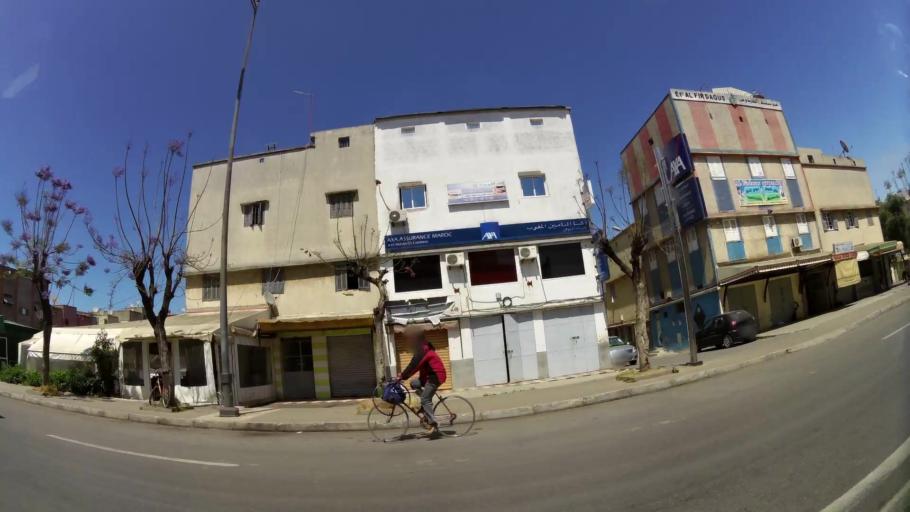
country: MA
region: Gharb-Chrarda-Beni Hssen
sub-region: Kenitra Province
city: Kenitra
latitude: 34.2456
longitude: -6.5523
